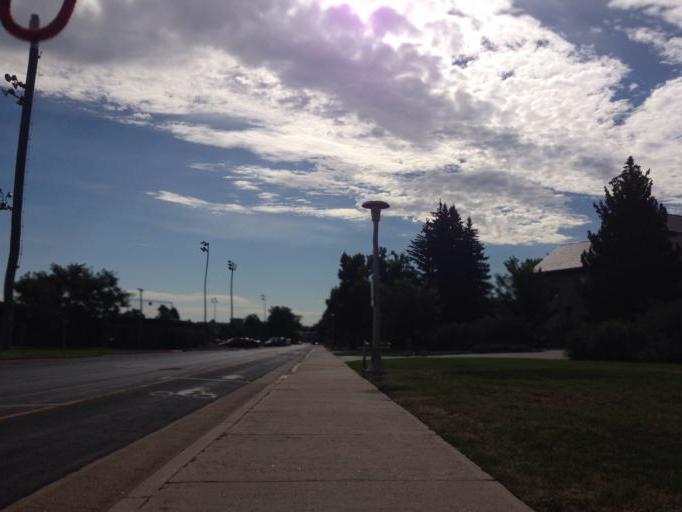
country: US
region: Colorado
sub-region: Larimer County
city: Fort Collins
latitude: 40.5726
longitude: -105.0912
